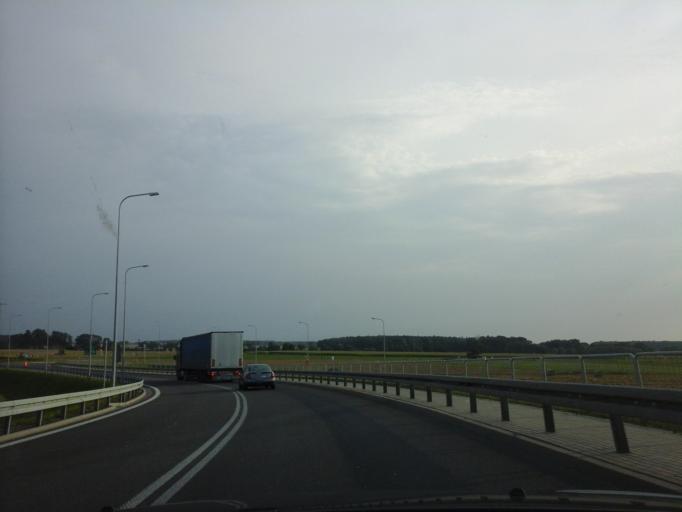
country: PL
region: Greater Poland Voivodeship
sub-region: Powiat leszczynski
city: Rydzyna
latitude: 51.7438
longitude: 16.6753
